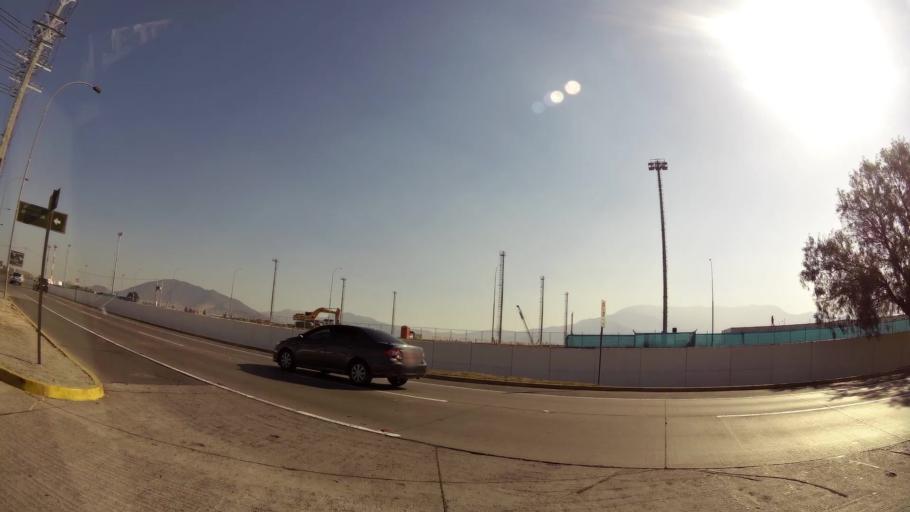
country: CL
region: Santiago Metropolitan
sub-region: Provincia de Santiago
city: Lo Prado
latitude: -33.4024
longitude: -70.7948
